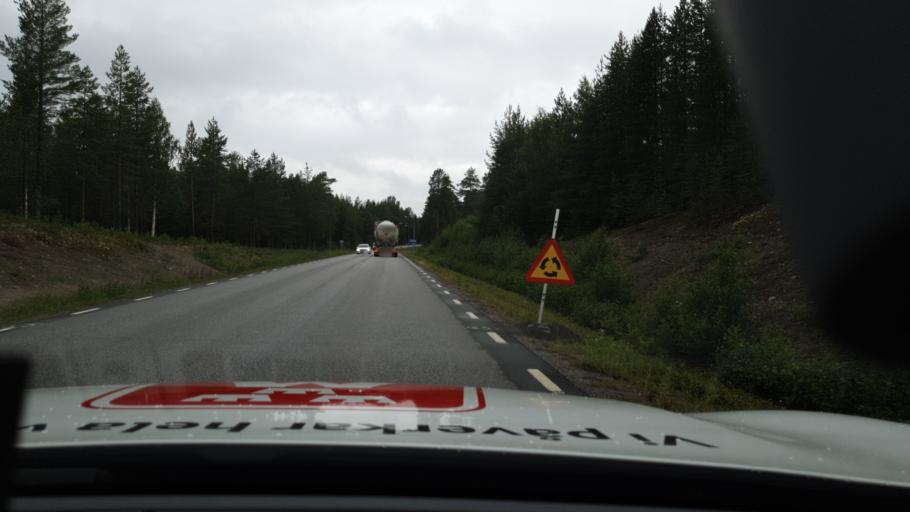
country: SE
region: Norrbotten
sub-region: Lulea Kommun
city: Ranea
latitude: 65.8616
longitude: 22.3158
